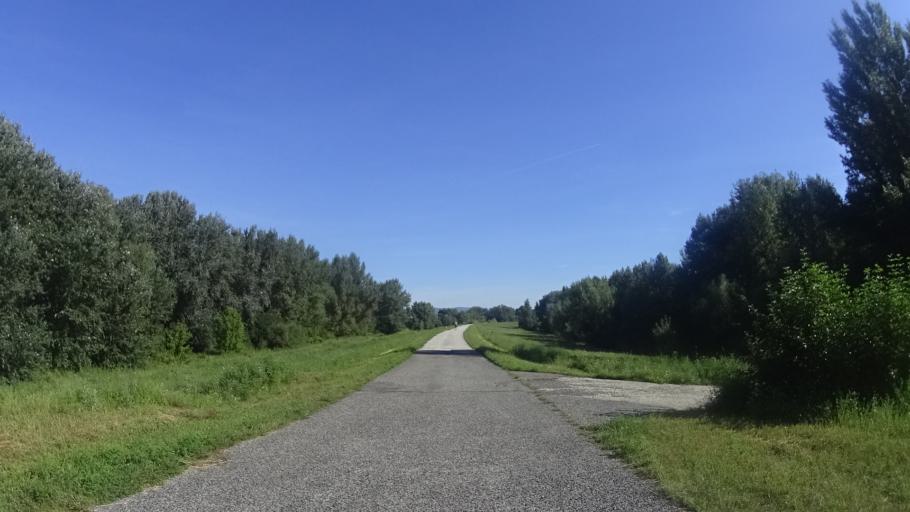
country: SK
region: Bratislavsky
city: Bratislava
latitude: 48.1118
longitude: 17.1463
